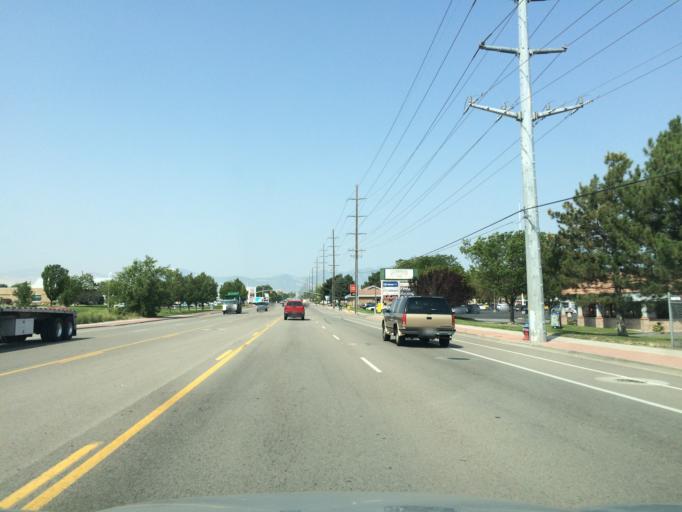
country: US
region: Utah
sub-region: Salt Lake County
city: South Jordan Heights
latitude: 40.5878
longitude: -111.9544
